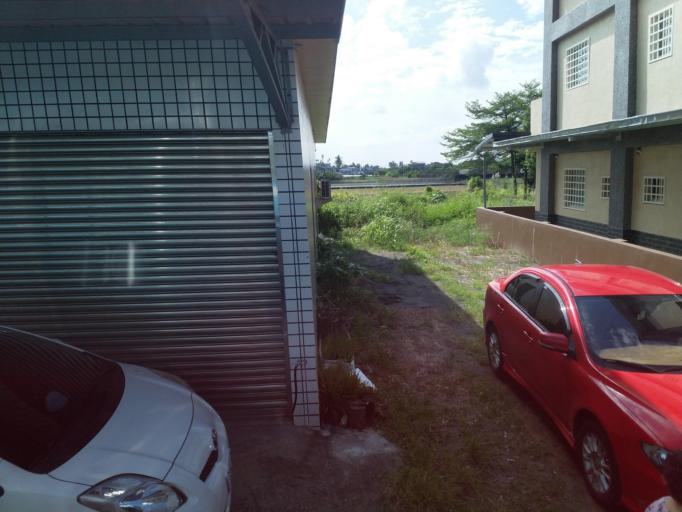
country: TW
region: Taiwan
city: Yujing
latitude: 22.9033
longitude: 120.5228
